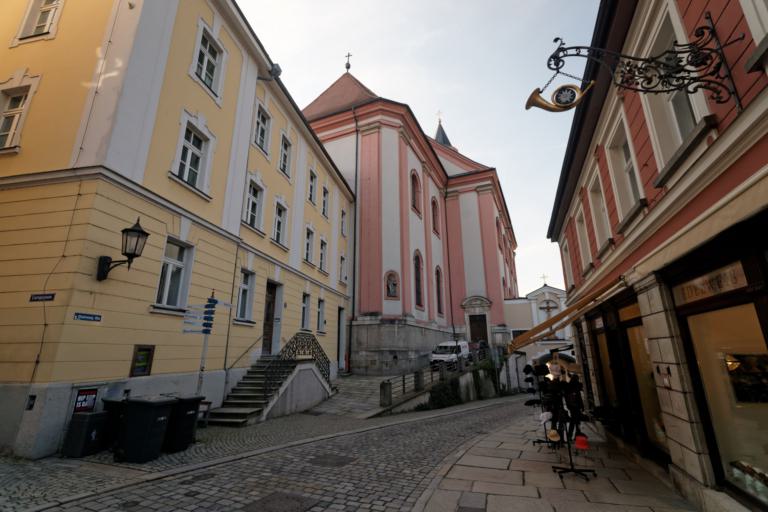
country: DE
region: Bavaria
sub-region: Lower Bavaria
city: Passau
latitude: 48.5755
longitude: 13.4633
